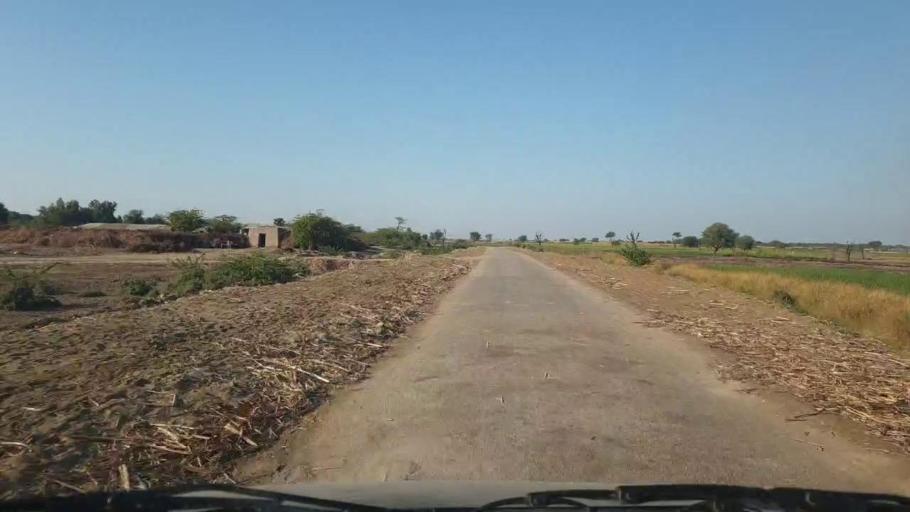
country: PK
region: Sindh
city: Samaro
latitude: 25.3459
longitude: 69.2993
